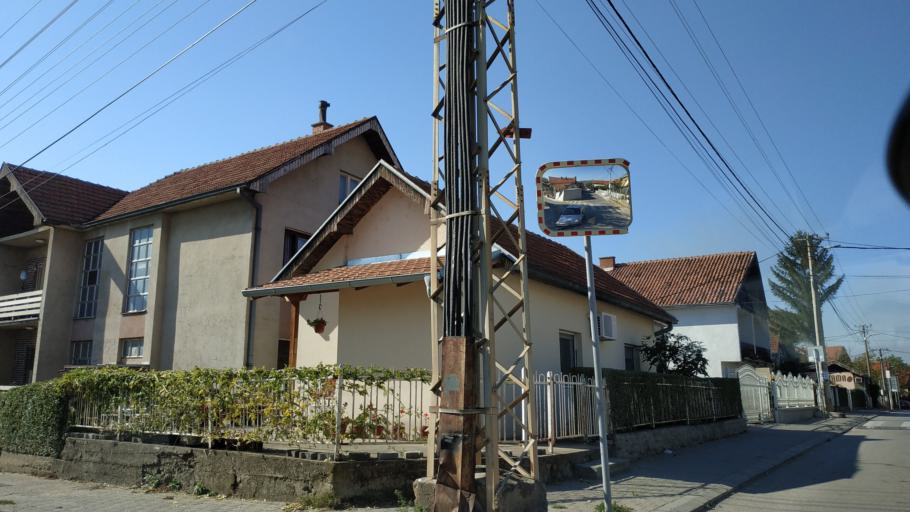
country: RS
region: Central Serbia
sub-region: Nisavski Okrug
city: Aleksinac
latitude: 43.5407
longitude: 21.6972
